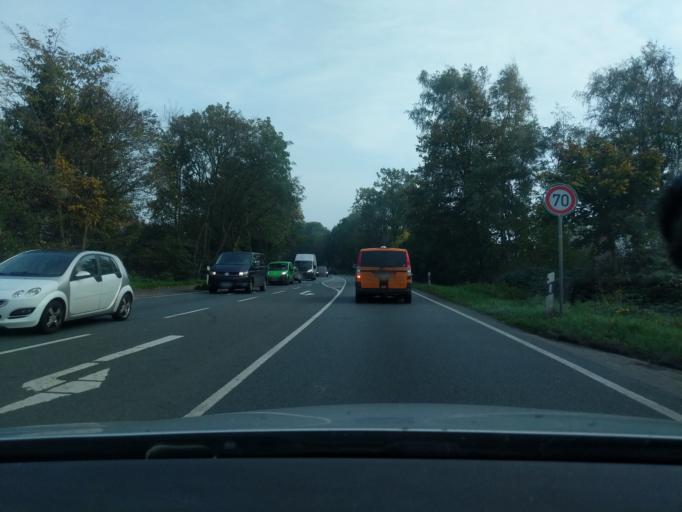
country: DE
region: Lower Saxony
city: Stade
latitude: 53.5861
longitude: 9.4590
